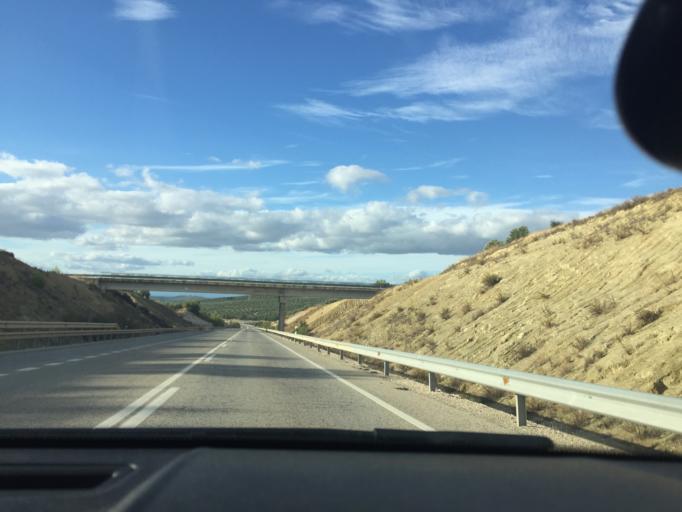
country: ES
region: Andalusia
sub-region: Provincia de Jaen
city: Torredonjimeno
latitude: 37.7623
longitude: -3.9669
